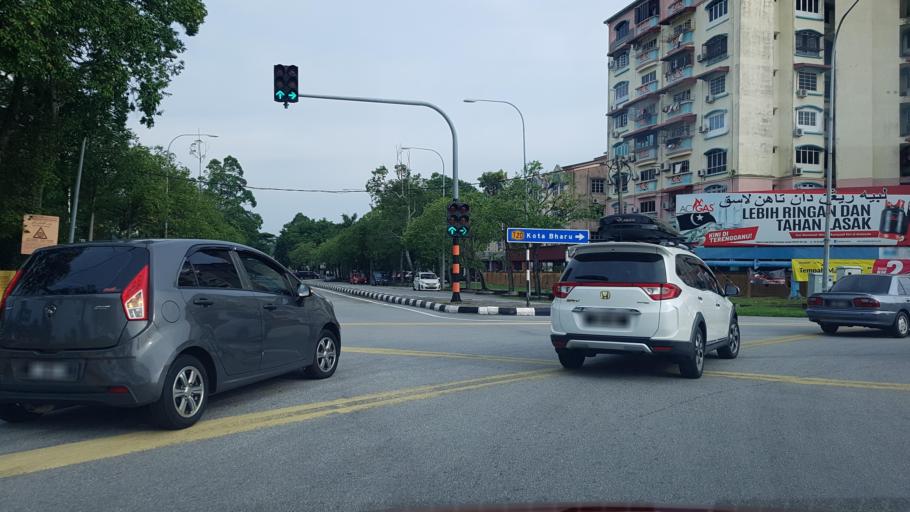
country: MY
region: Terengganu
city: Kuala Terengganu
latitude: 5.3266
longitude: 103.1386
